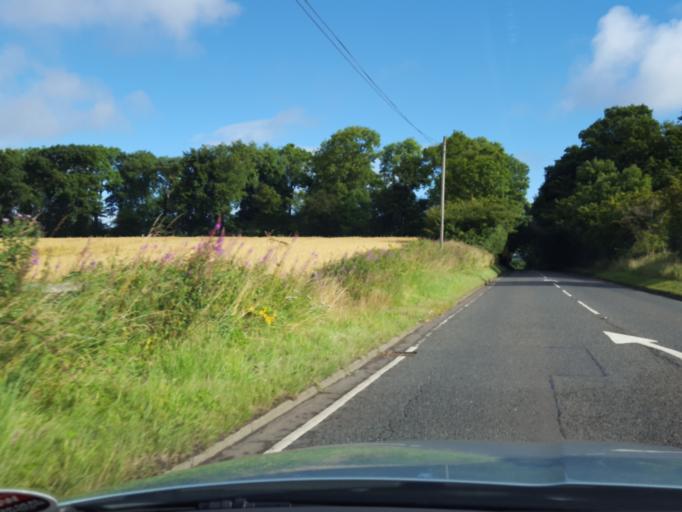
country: GB
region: Scotland
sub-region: West Lothian
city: Broxburn
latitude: 55.9590
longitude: -3.5093
